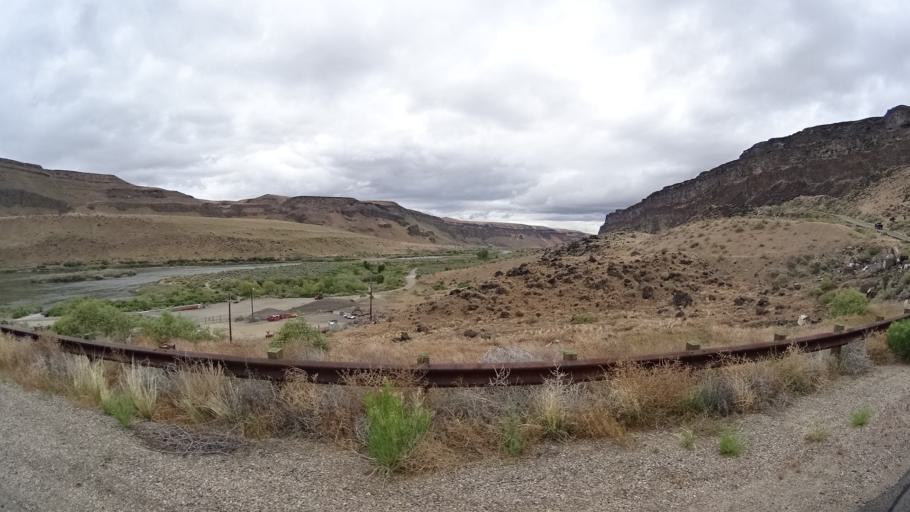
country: US
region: Idaho
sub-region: Owyhee County
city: Murphy
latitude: 43.2462
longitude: -116.3760
